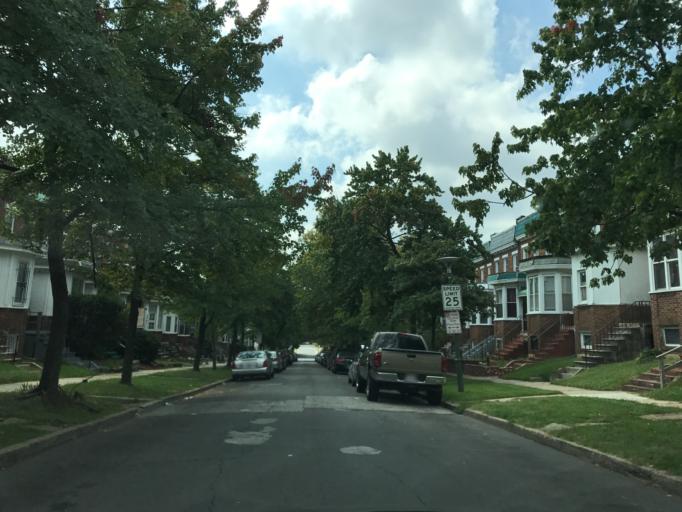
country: US
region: Maryland
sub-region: City of Baltimore
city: Baltimore
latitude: 39.3198
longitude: -76.5978
